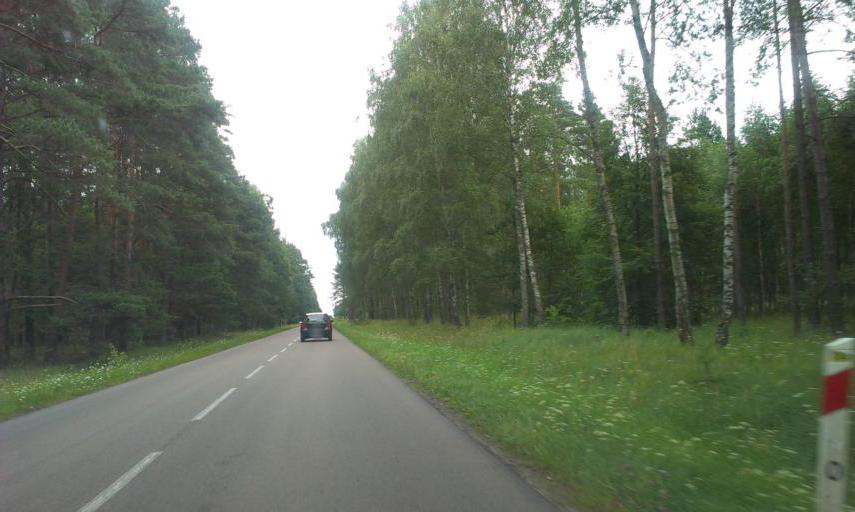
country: PL
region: West Pomeranian Voivodeship
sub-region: Powiat szczecinecki
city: Barwice
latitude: 53.7552
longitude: 16.2659
